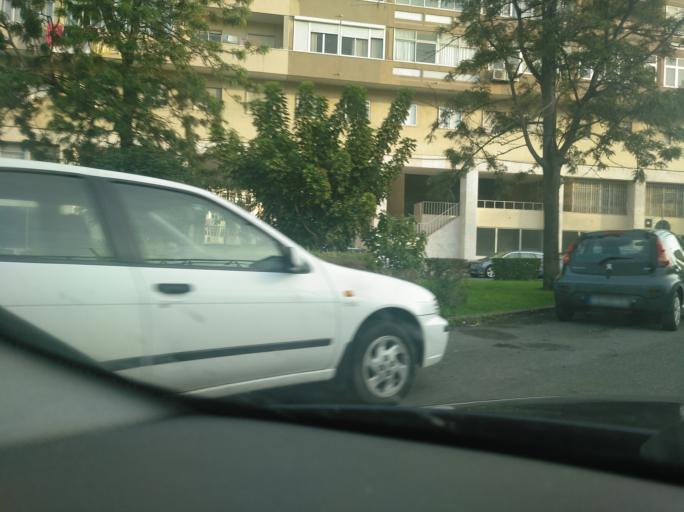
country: PT
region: Lisbon
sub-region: Odivelas
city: Olival do Basto
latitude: 38.7809
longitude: -9.1655
